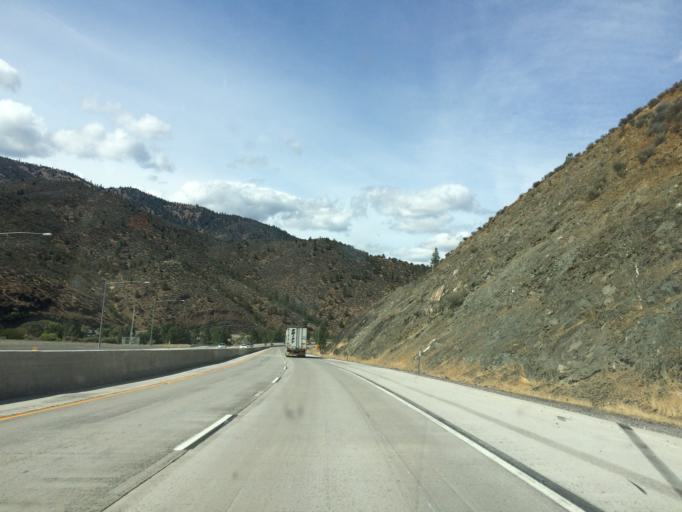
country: US
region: California
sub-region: Siskiyou County
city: Montague
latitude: 41.8505
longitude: -122.5686
